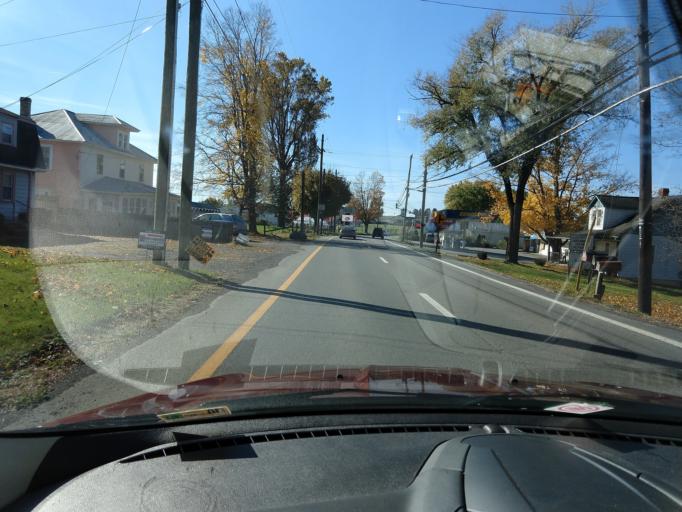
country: US
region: West Virginia
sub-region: Greenbrier County
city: Fairlea
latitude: 37.7809
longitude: -80.4591
